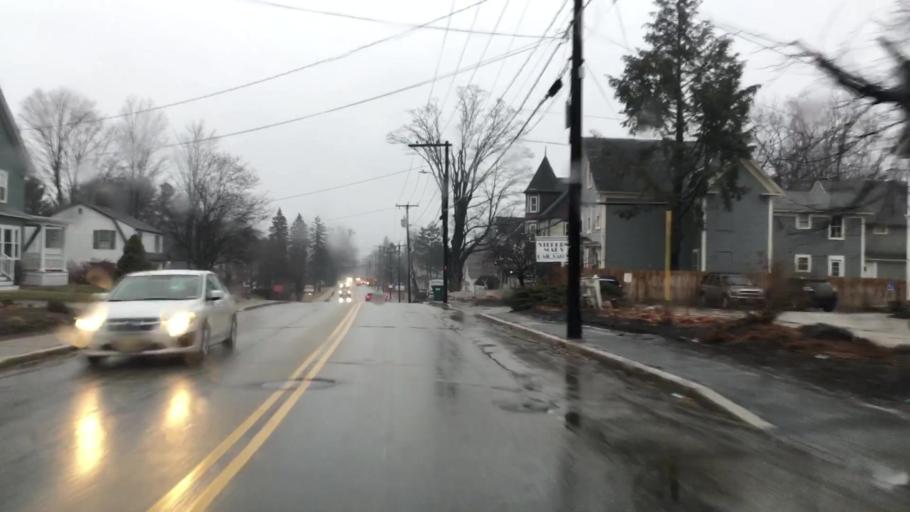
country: US
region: New Hampshire
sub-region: Hillsborough County
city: Milford
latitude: 42.8317
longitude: -71.6411
